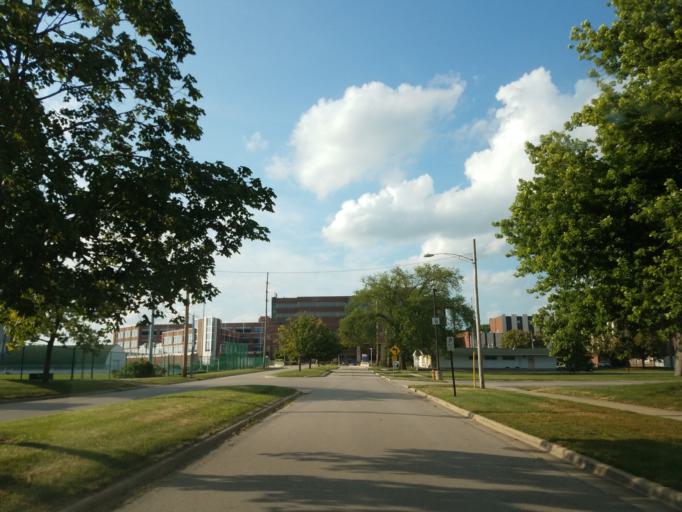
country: US
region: Illinois
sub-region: McLean County
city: Bloomington
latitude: 40.4949
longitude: -88.9908
